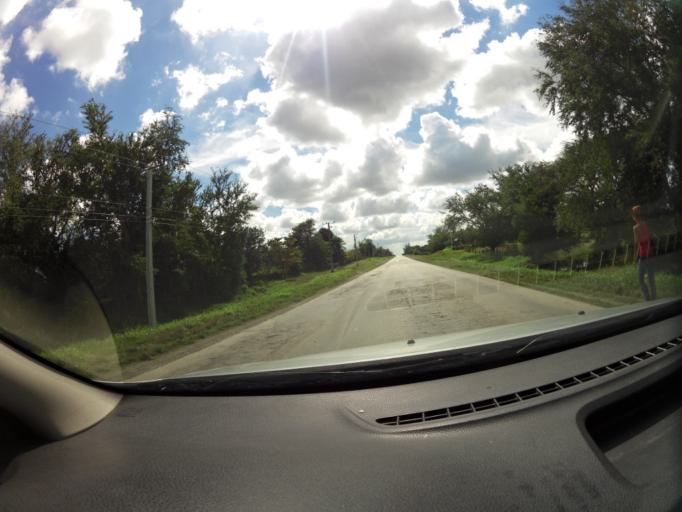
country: CU
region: Las Tunas
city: Las Tunas
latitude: 20.8447
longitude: -76.9112
